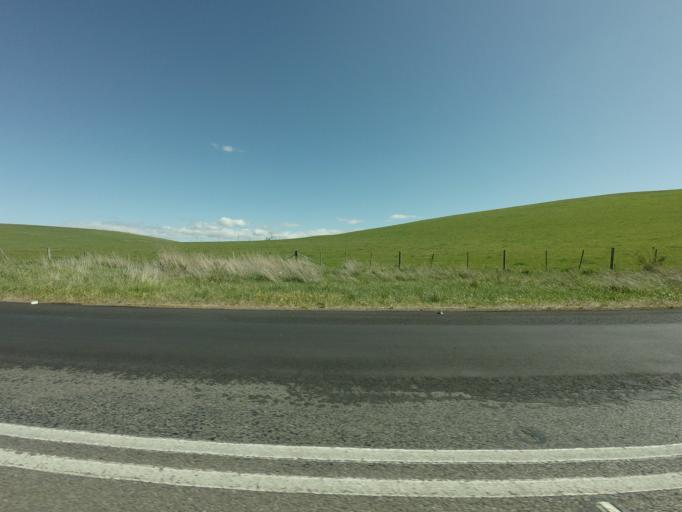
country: AU
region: Tasmania
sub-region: Derwent Valley
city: New Norfolk
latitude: -42.6482
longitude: 146.9258
